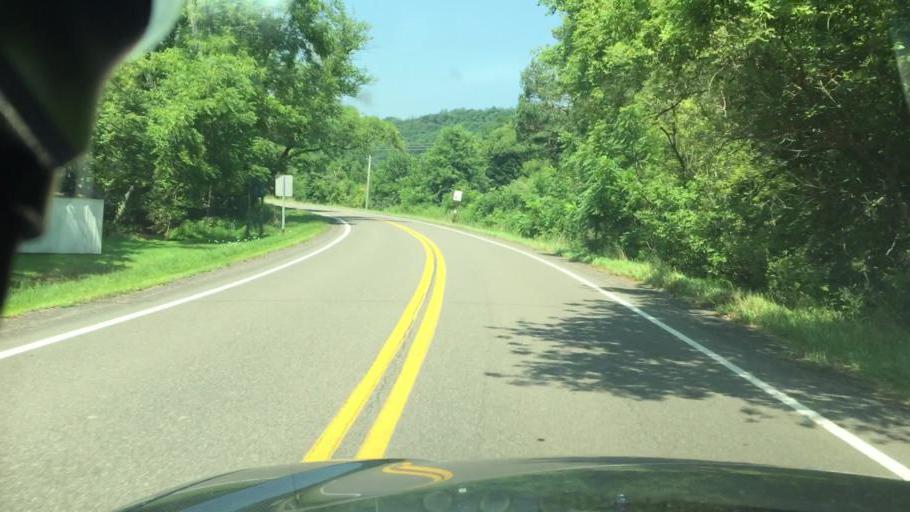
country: US
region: Pennsylvania
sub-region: Columbia County
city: Almedia
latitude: 40.9788
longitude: -76.3766
